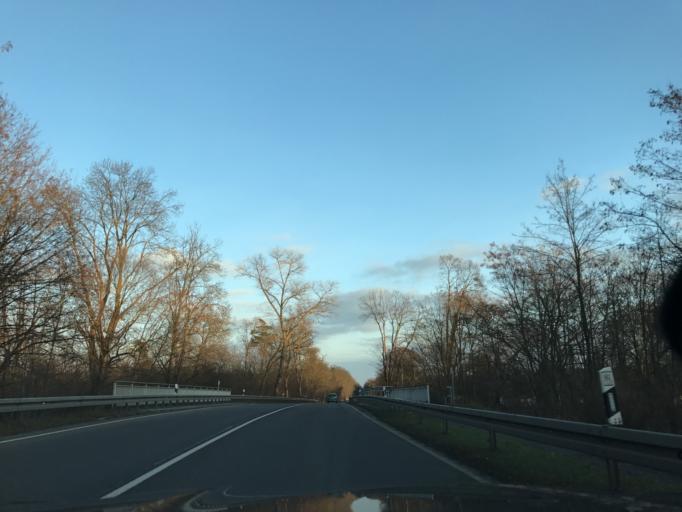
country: DE
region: Saxony-Anhalt
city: Genthin
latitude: 52.4118
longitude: 12.2250
